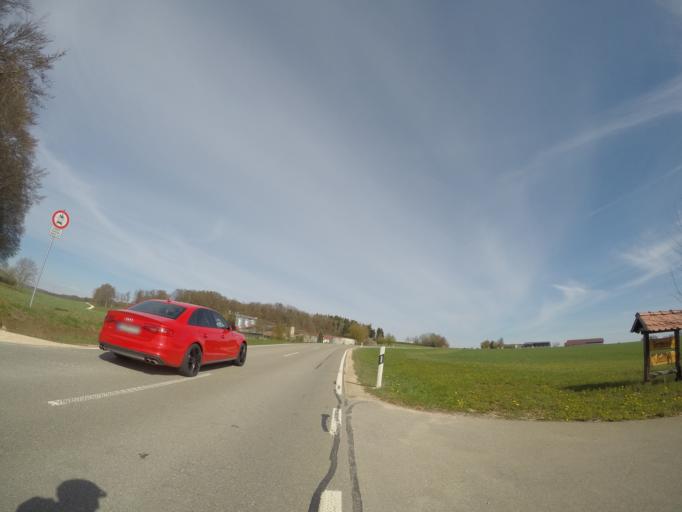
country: DE
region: Baden-Wuerttemberg
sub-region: Tuebingen Region
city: Laichingen
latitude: 48.5056
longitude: 9.6740
